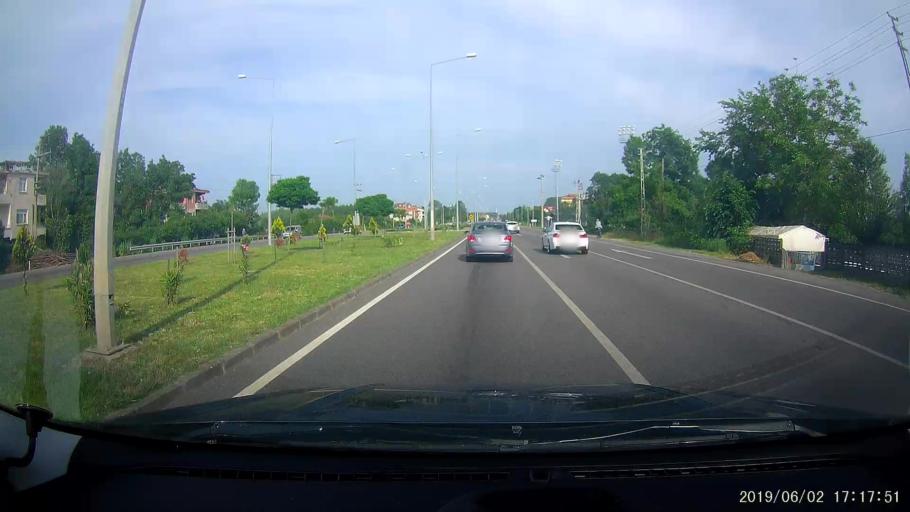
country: TR
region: Samsun
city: Dikbiyik
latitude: 41.2266
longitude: 36.5882
